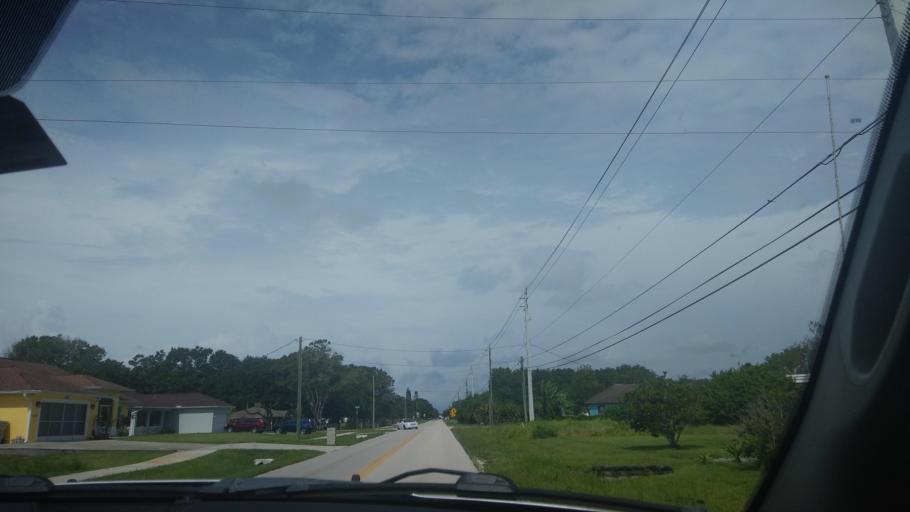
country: US
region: Florida
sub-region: Indian River County
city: Sebastian
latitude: 27.7526
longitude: -80.5144
